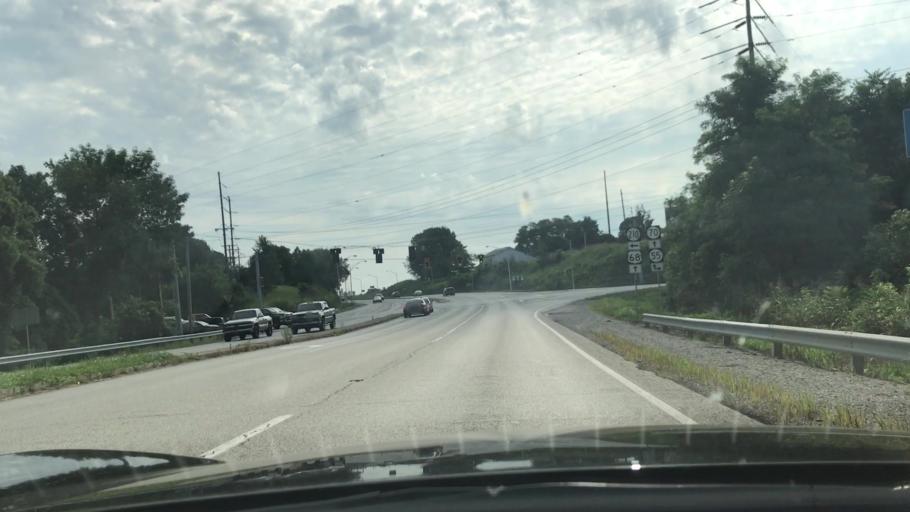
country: US
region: Kentucky
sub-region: Taylor County
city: Campbellsville
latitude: 37.3381
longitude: -85.3616
